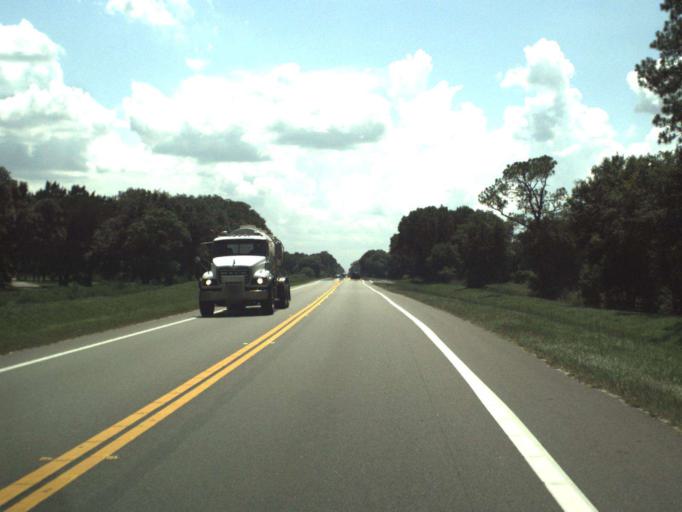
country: US
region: Florida
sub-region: Lake County
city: Mascotte
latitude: 28.5802
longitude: -81.9743
